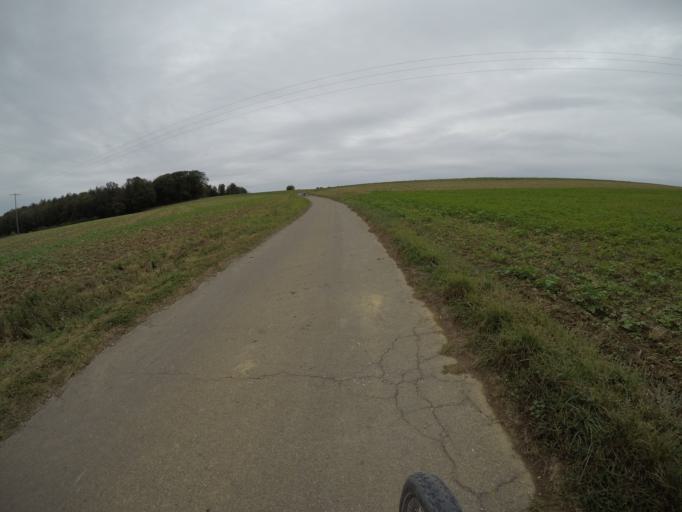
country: DE
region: Baden-Wuerttemberg
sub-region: Regierungsbezirk Stuttgart
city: Eberdingen
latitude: 48.8874
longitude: 8.9776
